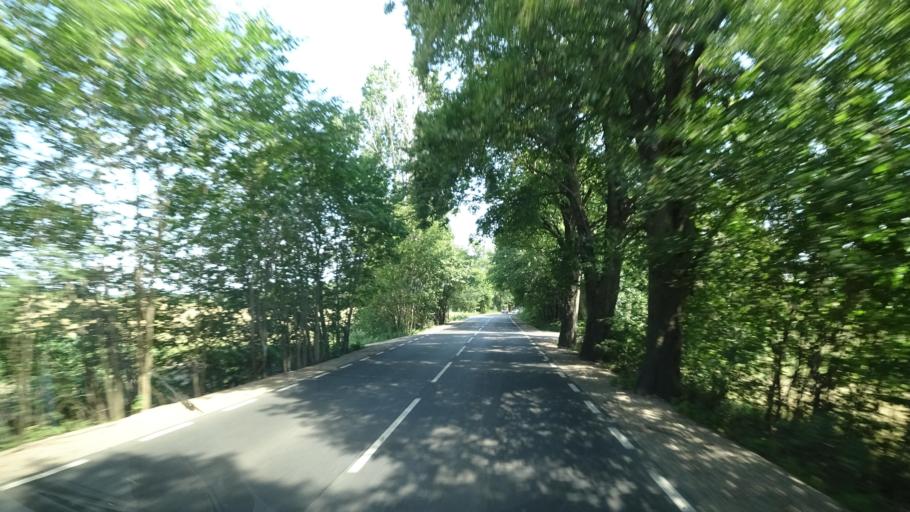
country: PL
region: Pomeranian Voivodeship
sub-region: Powiat koscierski
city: Dziemiany
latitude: 53.9668
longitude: 17.7557
